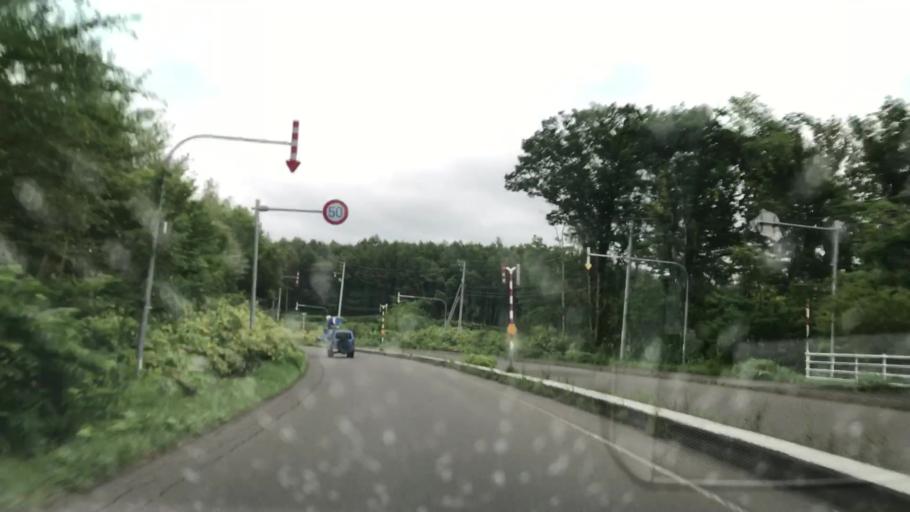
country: JP
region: Hokkaido
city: Niseko Town
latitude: 42.7960
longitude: 140.7432
